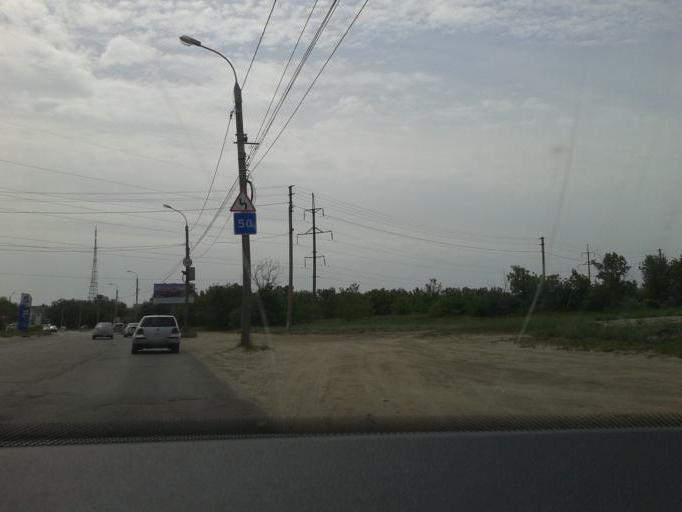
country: RU
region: Volgograd
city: Volgograd
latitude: 48.7548
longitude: 44.5241
